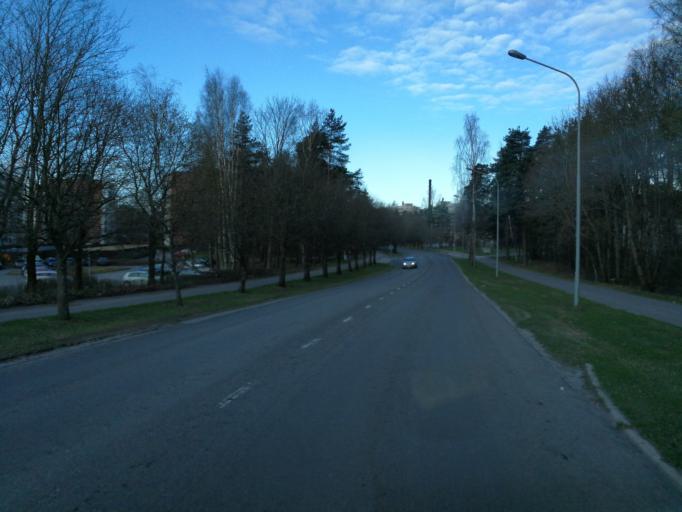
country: FI
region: Varsinais-Suomi
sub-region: Turku
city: Turku
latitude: 60.4339
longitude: 22.2952
